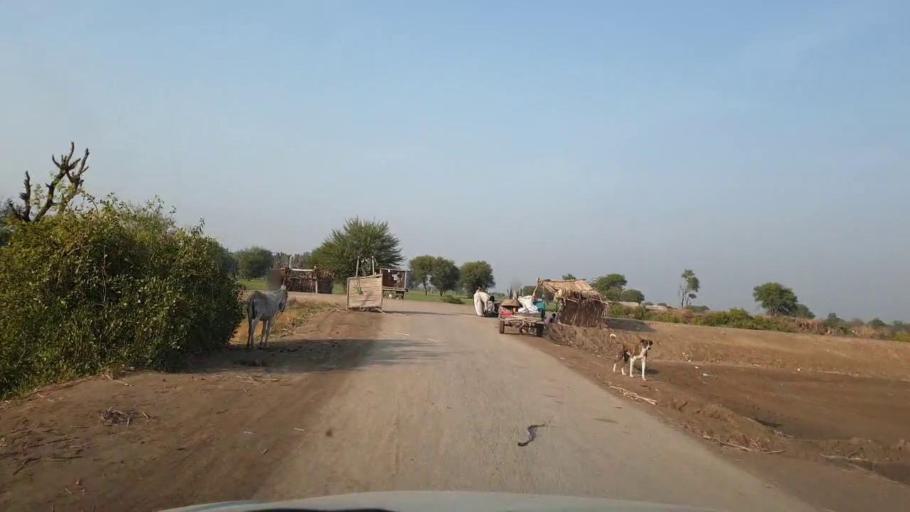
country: PK
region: Sindh
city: Pithoro
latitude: 25.6761
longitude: 69.2045
